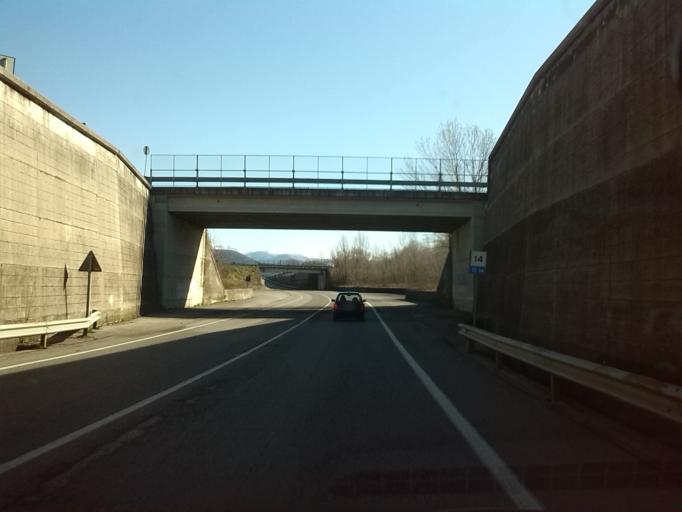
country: IT
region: Friuli Venezia Giulia
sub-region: Provincia di Udine
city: Premariacco
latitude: 46.0857
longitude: 13.4031
